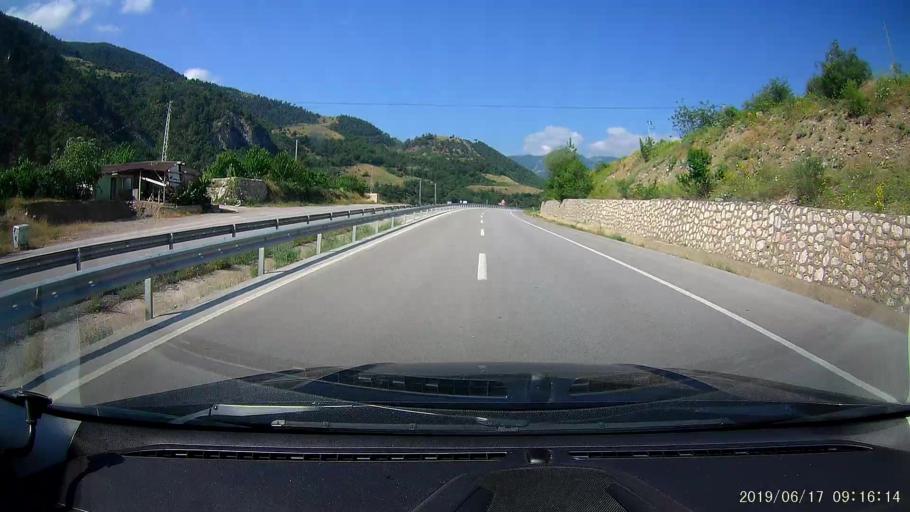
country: TR
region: Amasya
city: Akdag
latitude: 40.7455
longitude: 36.0169
